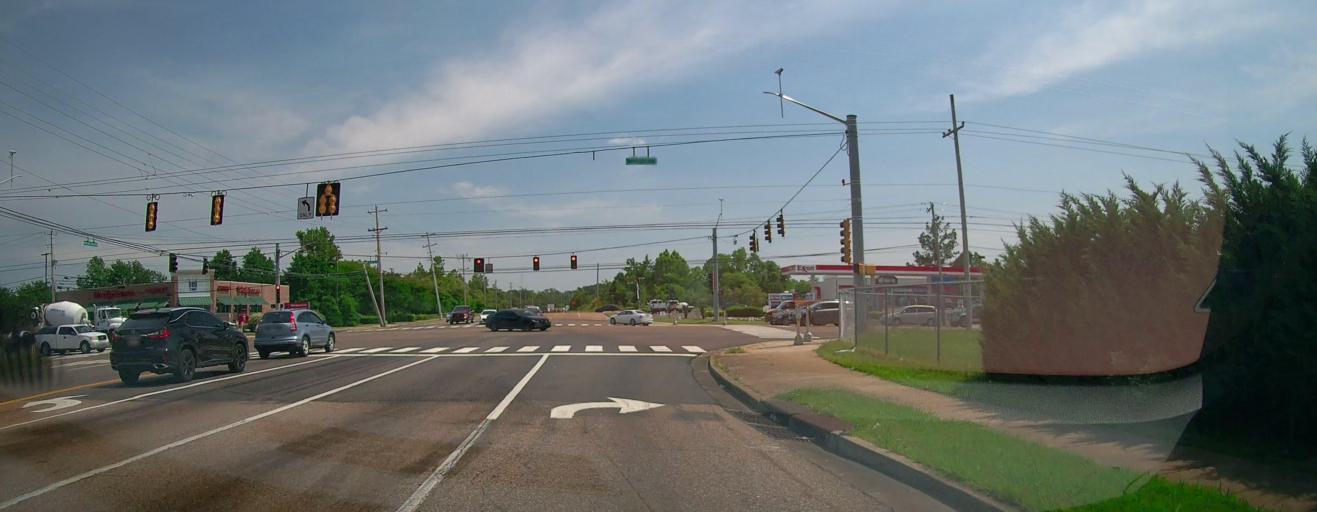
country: US
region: Tennessee
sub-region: Shelby County
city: Germantown
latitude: 35.0210
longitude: -89.7963
